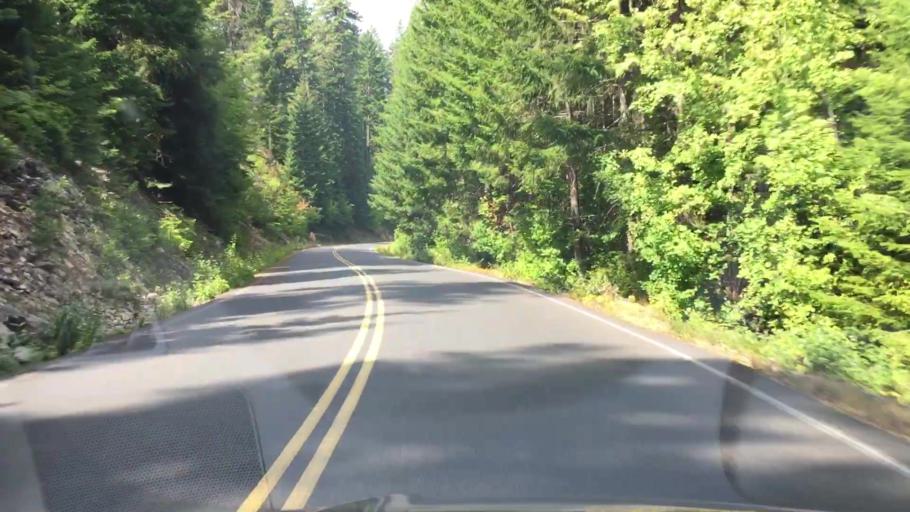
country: US
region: Washington
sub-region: Klickitat County
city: White Salmon
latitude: 46.0508
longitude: -121.5570
